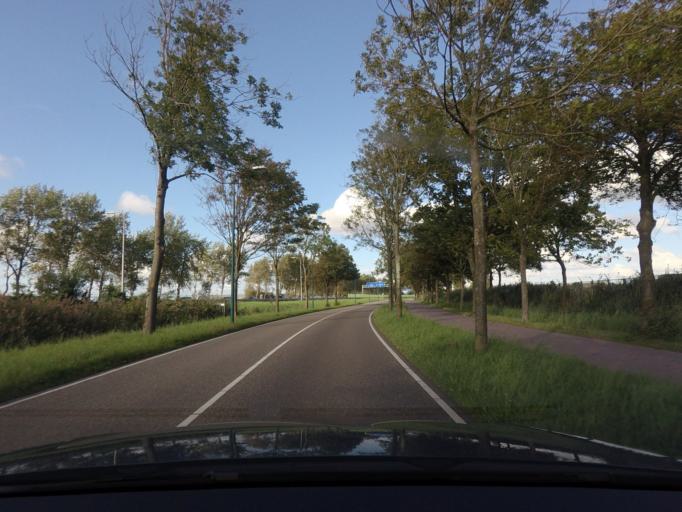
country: NL
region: South Holland
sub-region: Gemeente Oegstgeest
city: Oegstgeest
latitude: 52.1995
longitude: 4.4747
